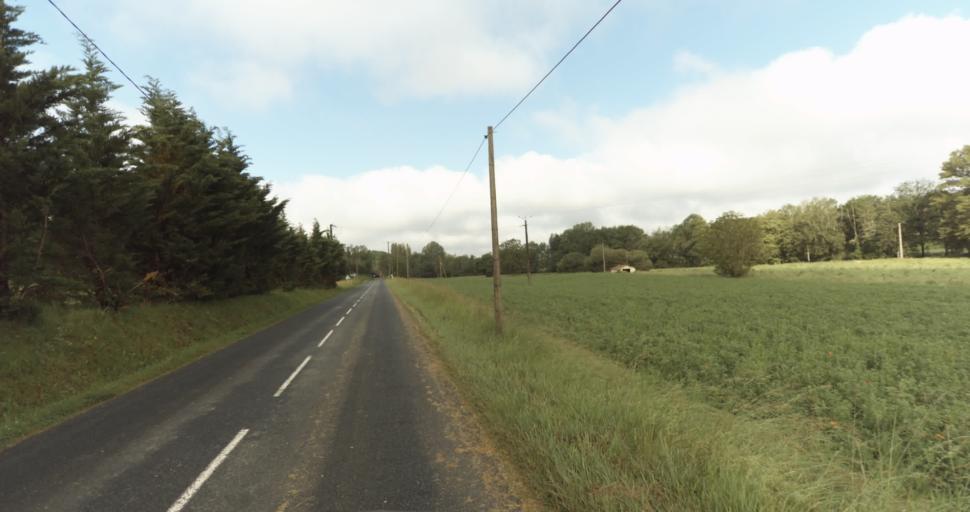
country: FR
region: Aquitaine
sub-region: Departement de la Dordogne
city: Lalinde
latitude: 44.9284
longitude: 0.7611
